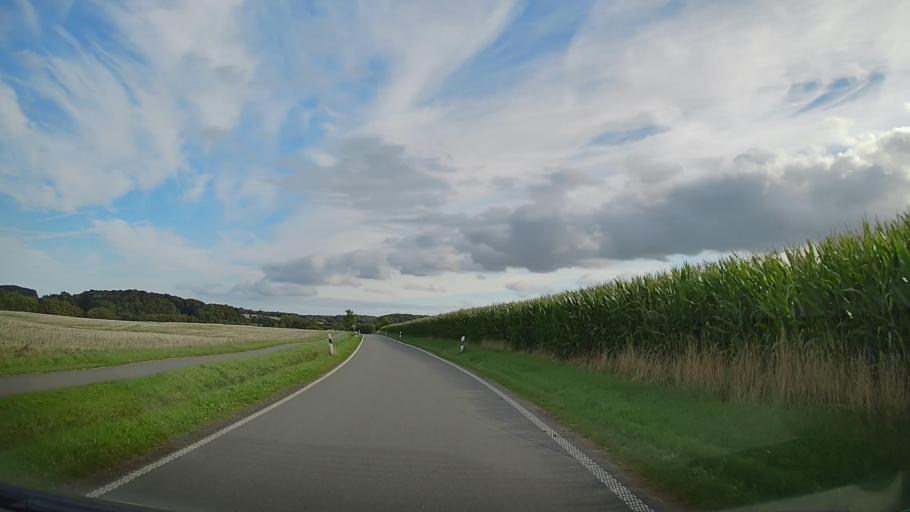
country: DE
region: Schleswig-Holstein
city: Westerholz
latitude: 54.8086
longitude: 9.6799
